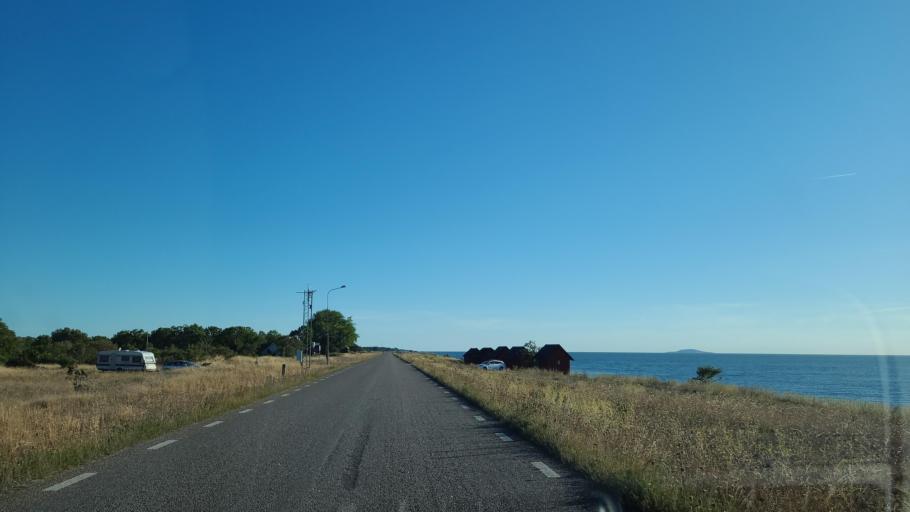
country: SE
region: Kalmar
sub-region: Vasterviks Kommun
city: Vaestervik
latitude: 57.3392
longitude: 17.0160
